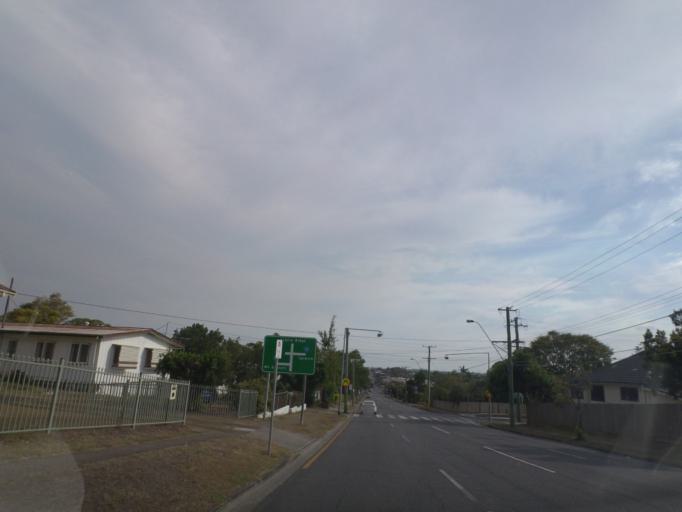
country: AU
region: Queensland
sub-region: Brisbane
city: Coopers Plains
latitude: -27.5554
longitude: 153.0410
